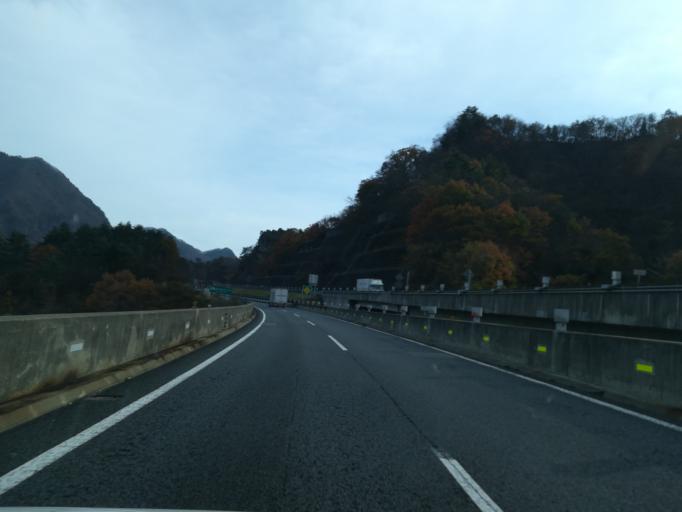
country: JP
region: Nagano
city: Saku
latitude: 36.3123
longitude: 138.6783
